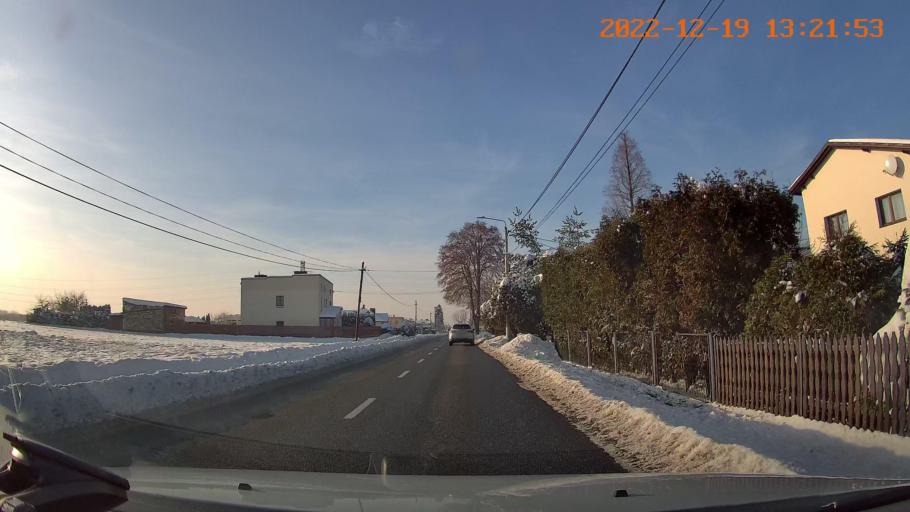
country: PL
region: Silesian Voivodeship
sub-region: Powiat bierunsko-ledzinski
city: Chelm Slaski
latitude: 50.1080
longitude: 19.1776
